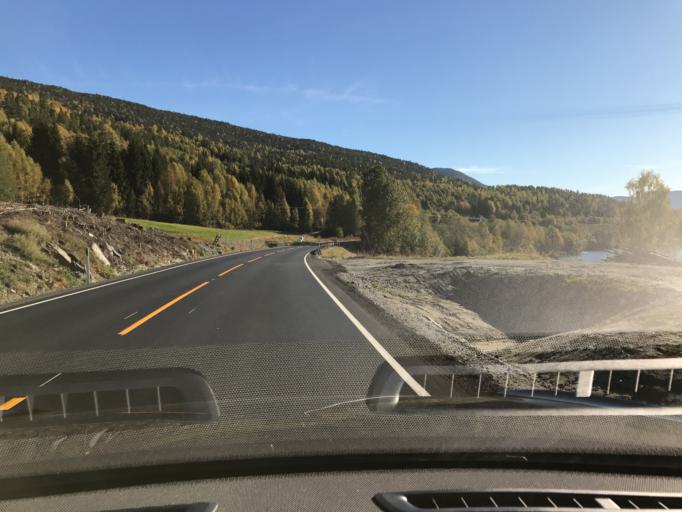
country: NO
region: Buskerud
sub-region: Krodsherad
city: Noresund
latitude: 60.3436
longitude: 9.6449
